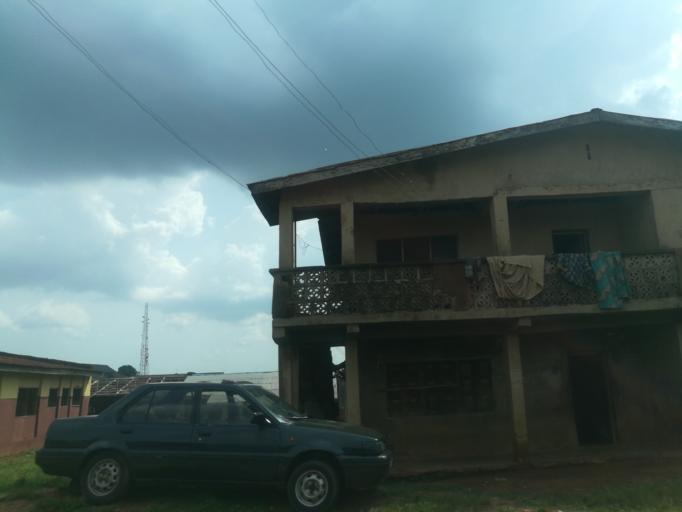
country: NG
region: Oyo
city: Moniya
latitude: 7.4650
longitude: 3.9175
